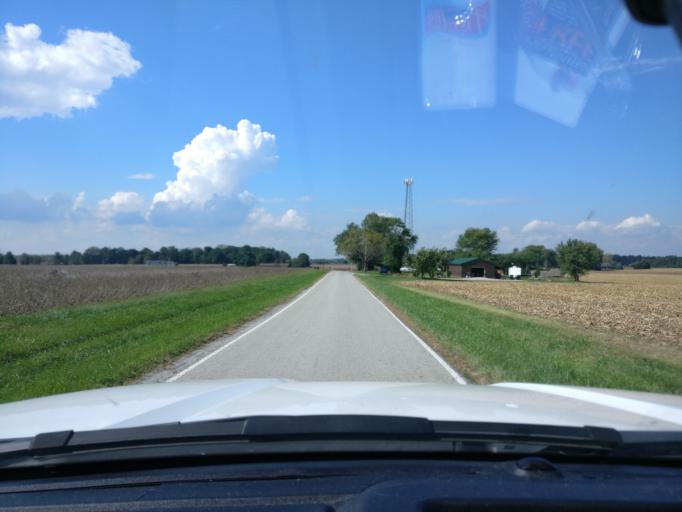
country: US
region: Ohio
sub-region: Warren County
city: Waynesville
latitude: 39.4645
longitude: -83.9889
